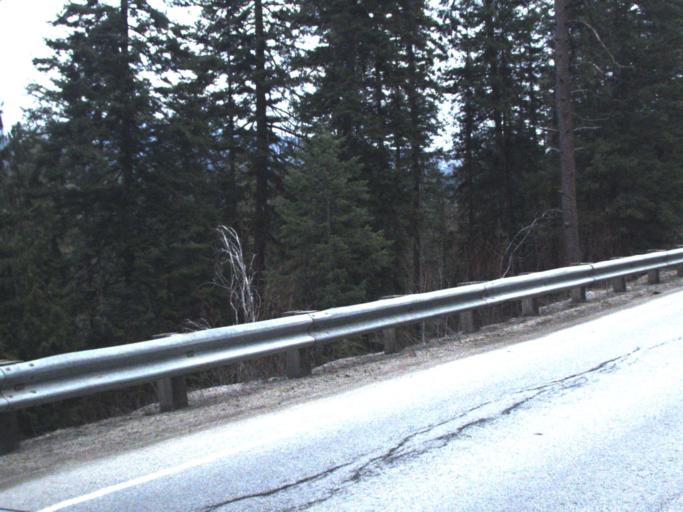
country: US
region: Washington
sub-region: Pend Oreille County
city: Newport
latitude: 48.2092
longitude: -117.0657
